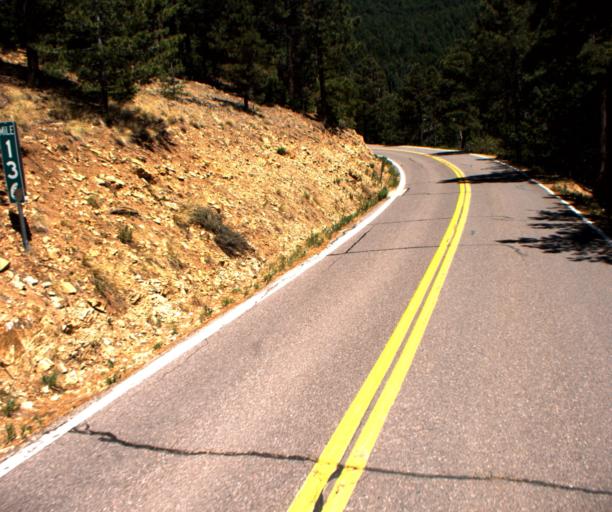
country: US
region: Arizona
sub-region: Graham County
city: Swift Trail Junction
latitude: 32.6572
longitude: -109.8646
